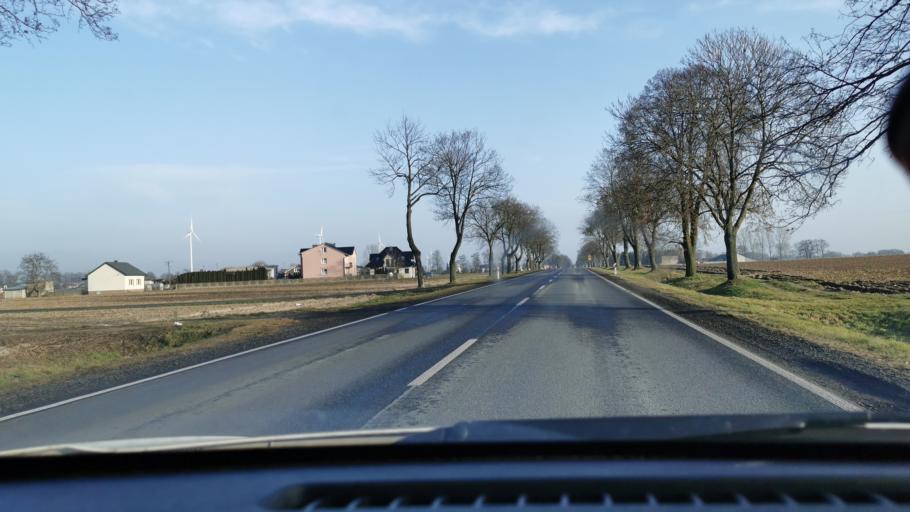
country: PL
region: Lodz Voivodeship
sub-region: Powiat sieradzki
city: Blaszki
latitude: 51.6382
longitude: 18.5143
